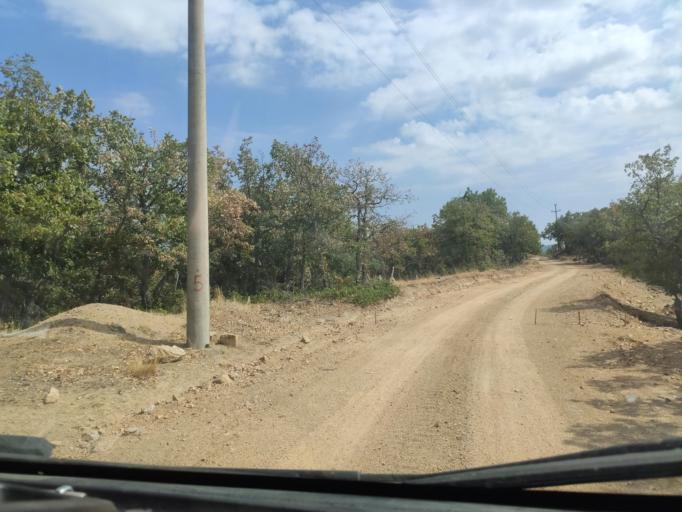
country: MK
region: Radovis
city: Radovish
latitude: 41.6665
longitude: 22.4074
